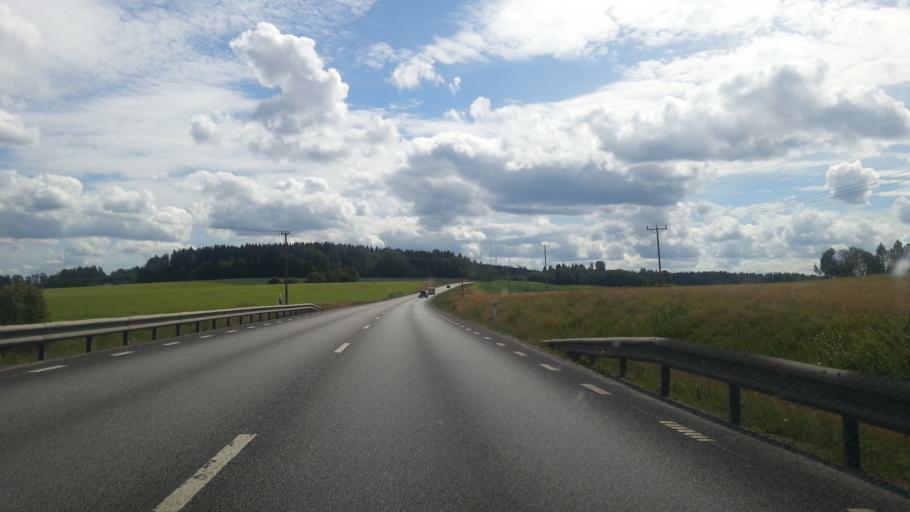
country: SE
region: OErebro
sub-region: Lindesbergs Kommun
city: Lindesberg
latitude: 59.5871
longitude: 15.1923
